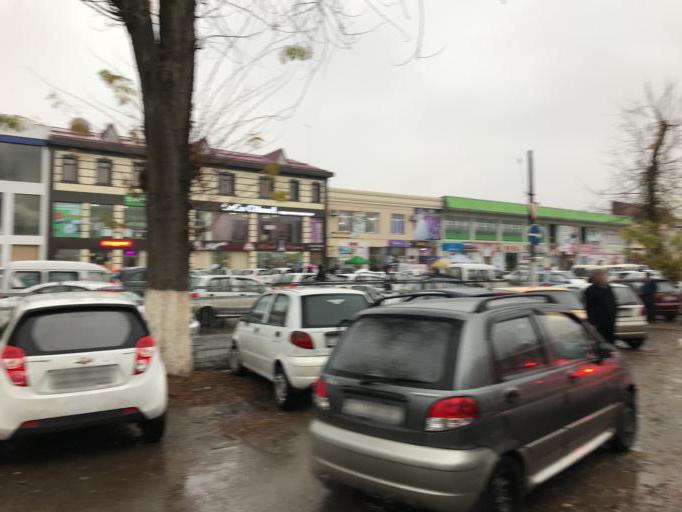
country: UZ
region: Toshkent
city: Yangiyul
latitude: 41.1163
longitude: 69.0559
